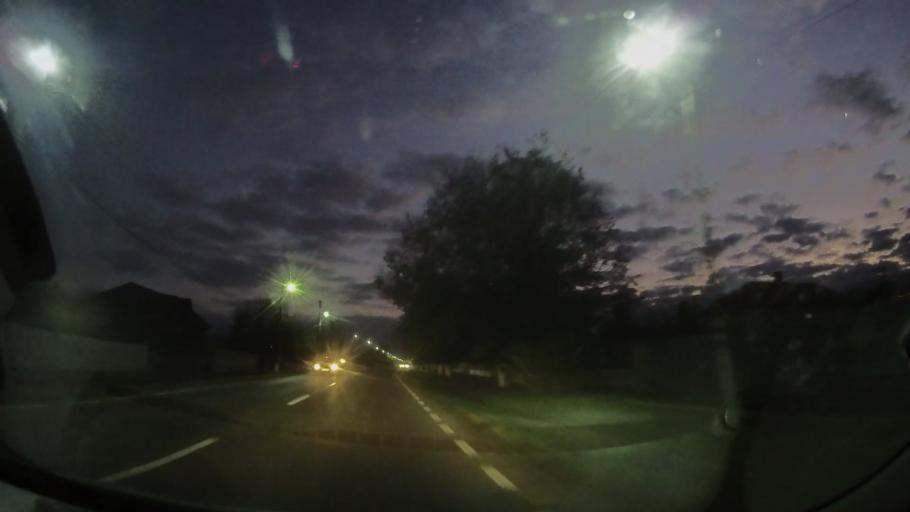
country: RO
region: Tulcea
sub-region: Comuna Mihail Kogalniceanu
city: Mihail Kogalniceanu
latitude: 45.0456
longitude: 28.7359
